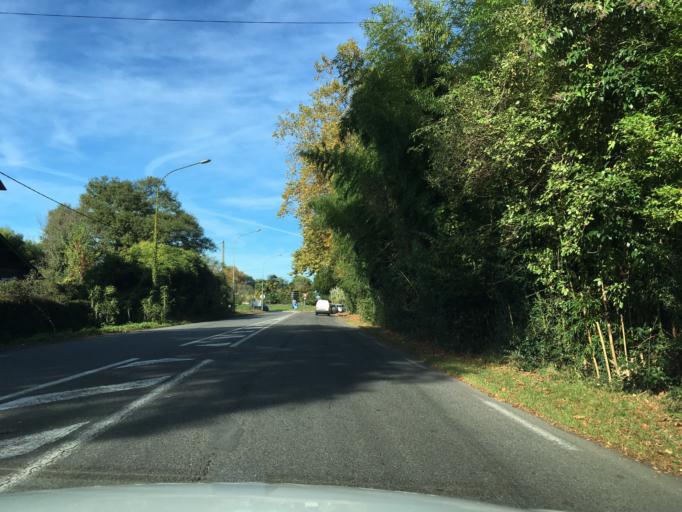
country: FR
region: Aquitaine
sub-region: Departement des Pyrenees-Atlantiques
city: Lons
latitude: 43.3369
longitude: -0.3797
